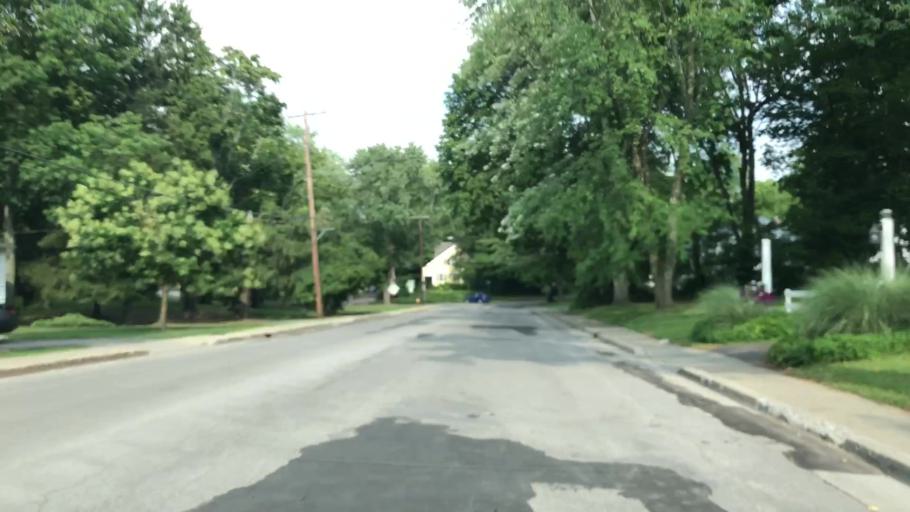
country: US
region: New York
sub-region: Erie County
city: East Aurora
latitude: 42.7725
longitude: -78.6093
